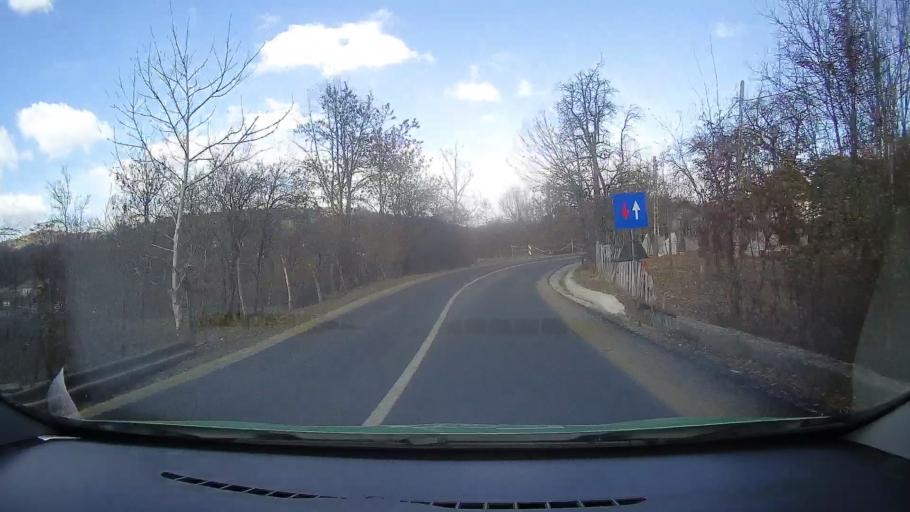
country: RO
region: Dambovita
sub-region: Comuna Runcu
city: Badeni
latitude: 45.1395
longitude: 25.4024
